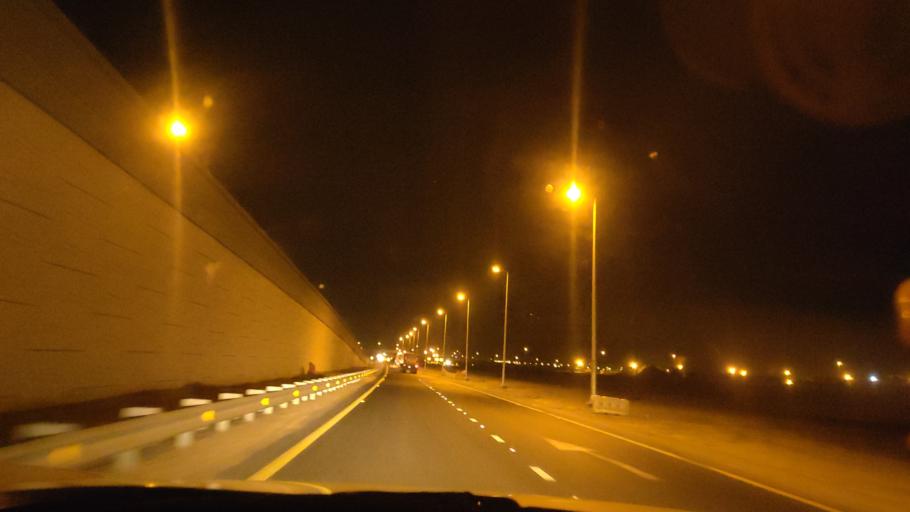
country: KW
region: Al Ahmadi
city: Al Fahahil
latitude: 28.9712
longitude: 48.1275
